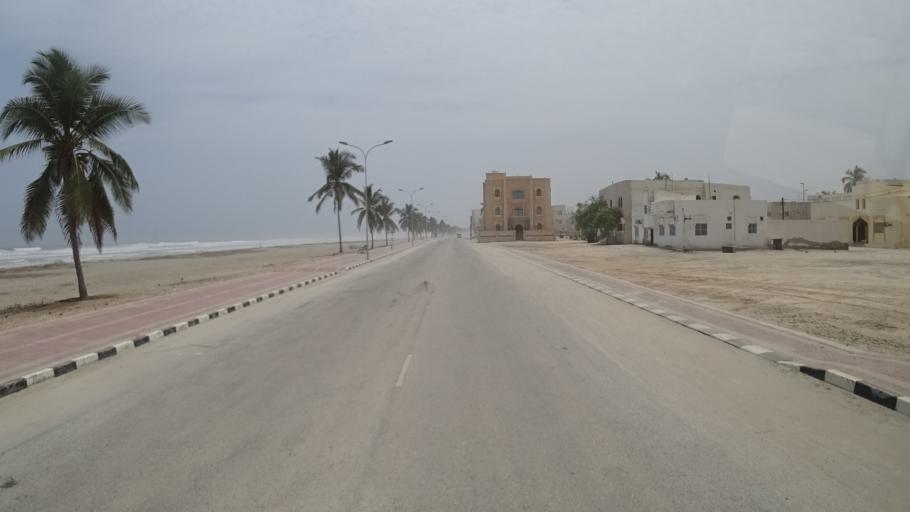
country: OM
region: Zufar
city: Salalah
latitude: 17.0344
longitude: 54.4005
